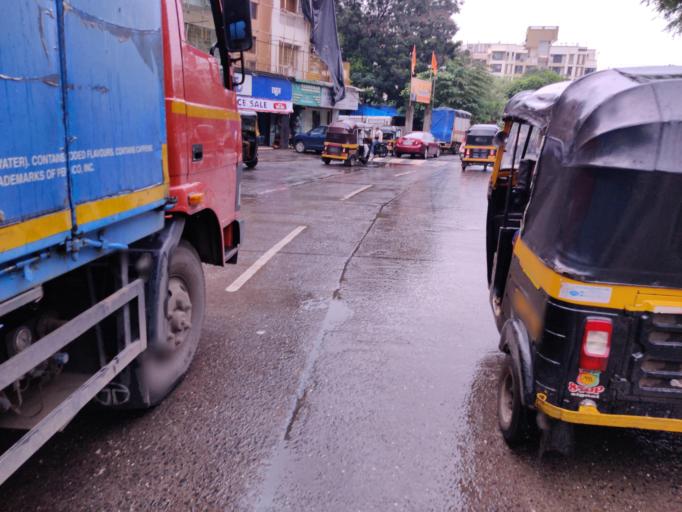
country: IN
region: Maharashtra
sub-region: Mumbai Suburban
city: Borivli
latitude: 19.2554
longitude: 72.8596
